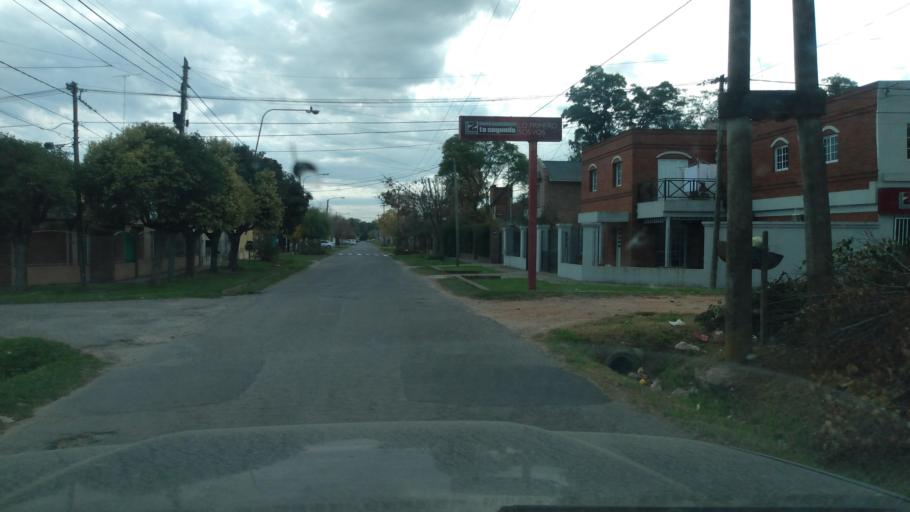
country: AR
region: Buenos Aires
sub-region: Partido de Lujan
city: Lujan
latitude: -34.5963
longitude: -59.1752
